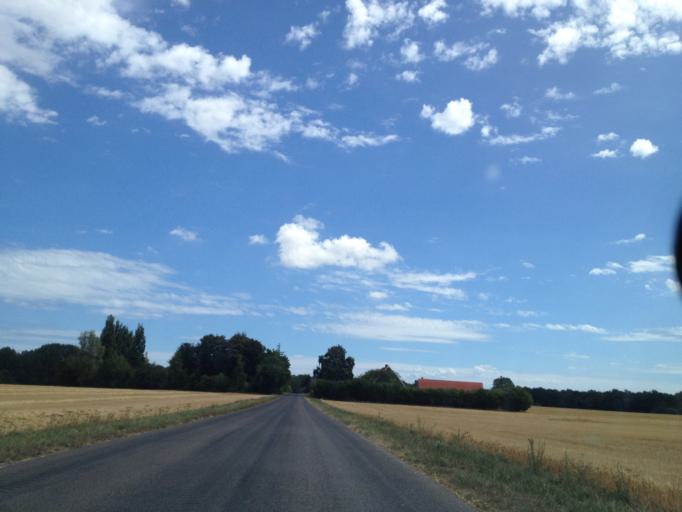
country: DK
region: Zealand
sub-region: Guldborgsund Kommune
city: Sakskobing
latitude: 54.7570
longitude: 11.6766
